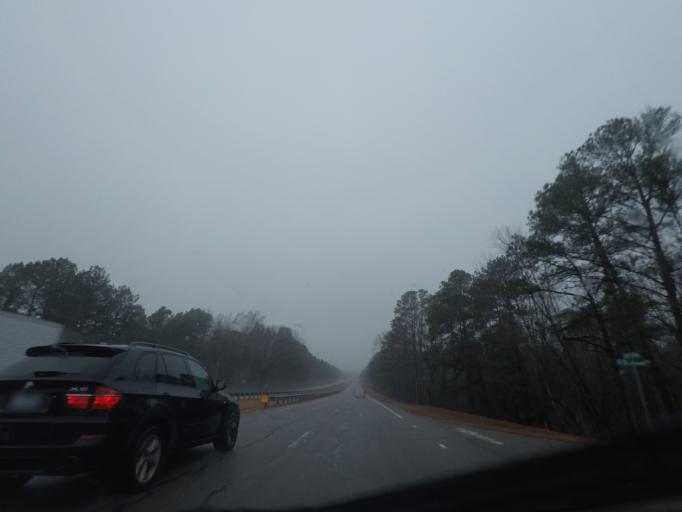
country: US
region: North Carolina
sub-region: Moore County
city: Southern Pines
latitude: 35.1967
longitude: -79.3766
